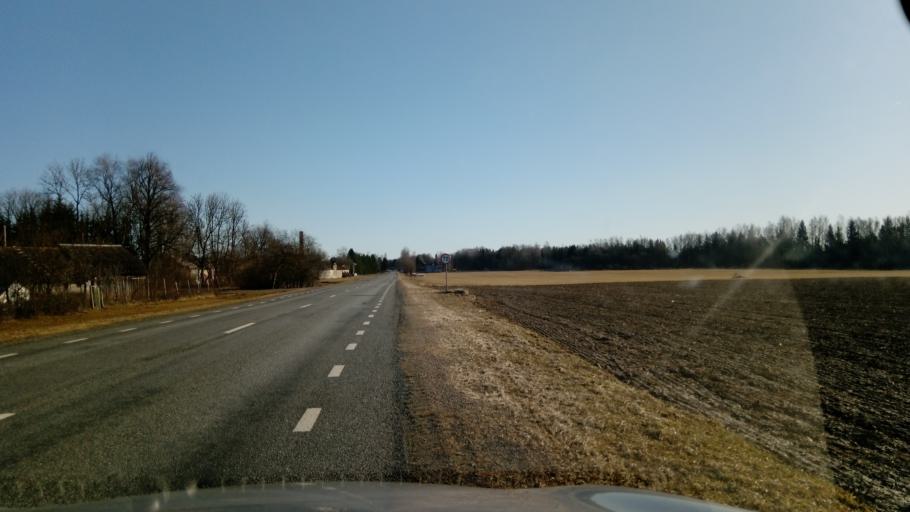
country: EE
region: Jaervamaa
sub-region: Jaerva-Jaani vald
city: Jarva-Jaani
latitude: 59.1041
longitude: 25.9957
